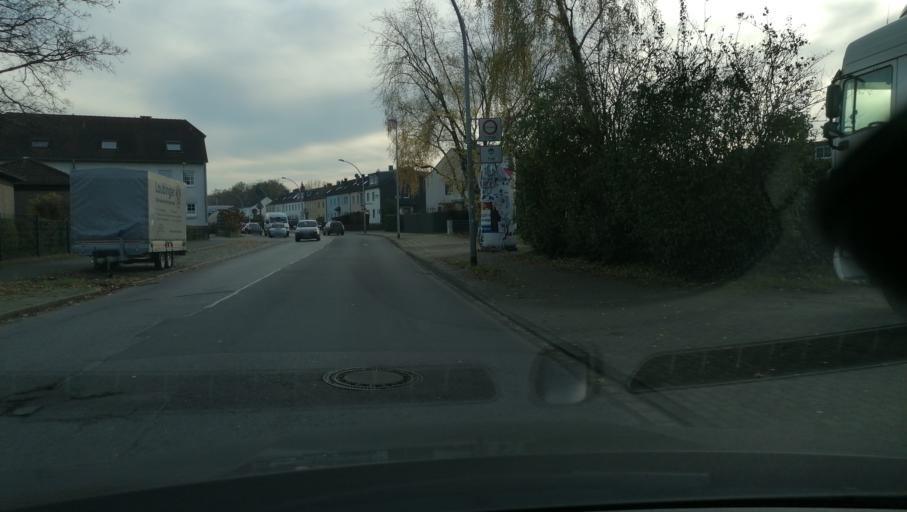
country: DE
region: North Rhine-Westphalia
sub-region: Regierungsbezirk Arnsberg
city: Herne
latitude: 51.5723
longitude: 7.2398
